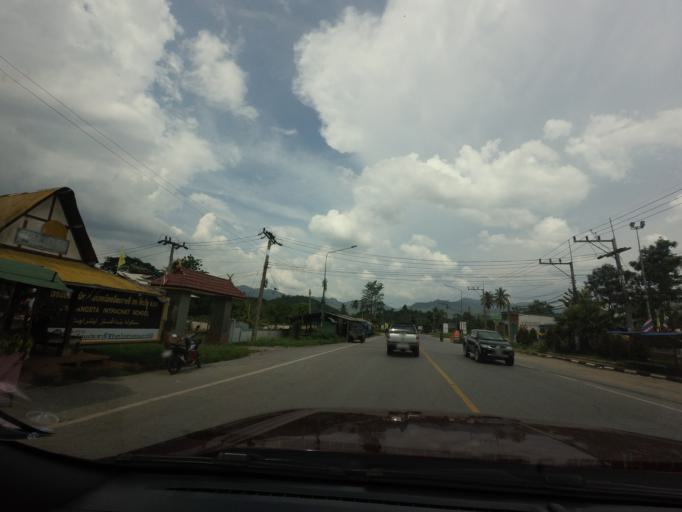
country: TH
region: Yala
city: Ban Nang Sata
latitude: 6.2664
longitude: 101.2667
